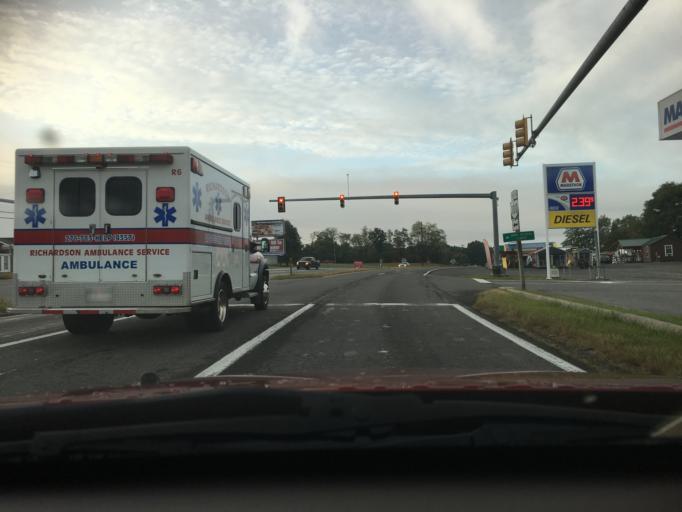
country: US
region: Virginia
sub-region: Pulaski County
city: Dublin
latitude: 37.0926
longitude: -80.6879
